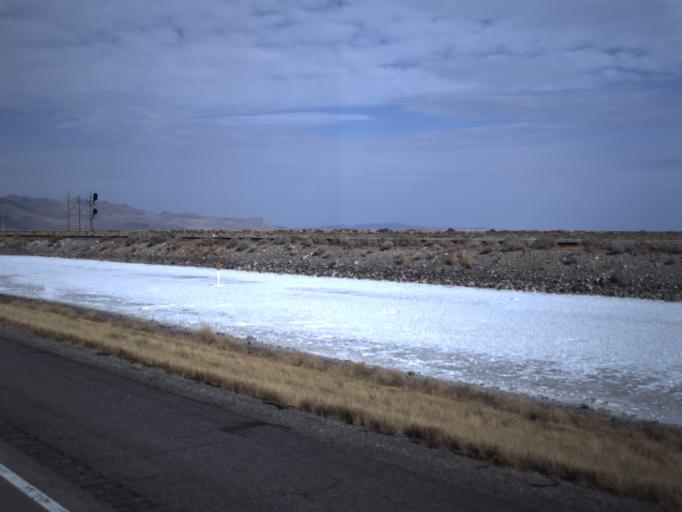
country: US
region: Utah
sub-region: Tooele County
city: Grantsville
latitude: 40.7415
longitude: -112.6266
